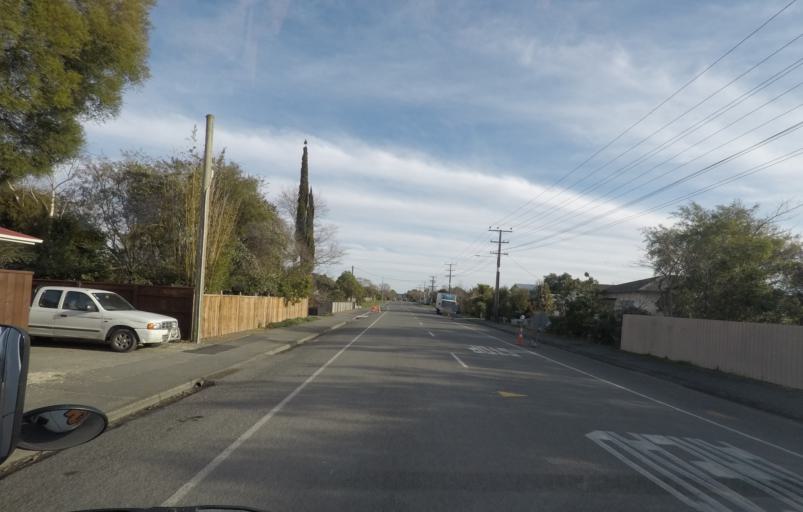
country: NZ
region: Tasman
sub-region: Tasman District
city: Brightwater
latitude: -41.3746
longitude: 173.1062
